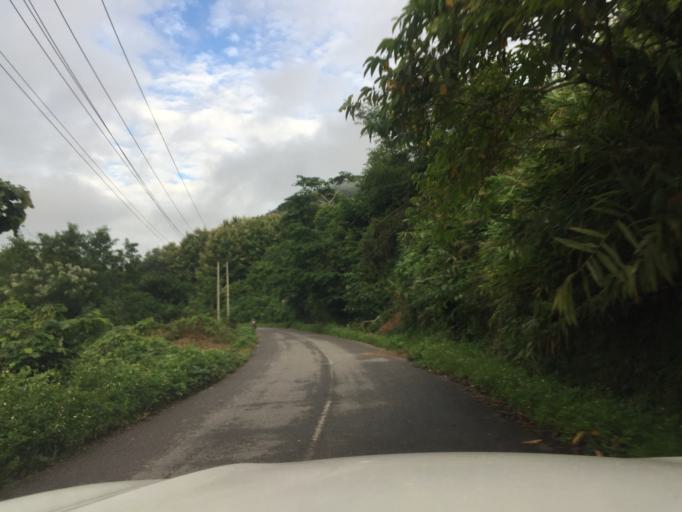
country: LA
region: Phongsali
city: Khoa
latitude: 21.1031
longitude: 102.2673
